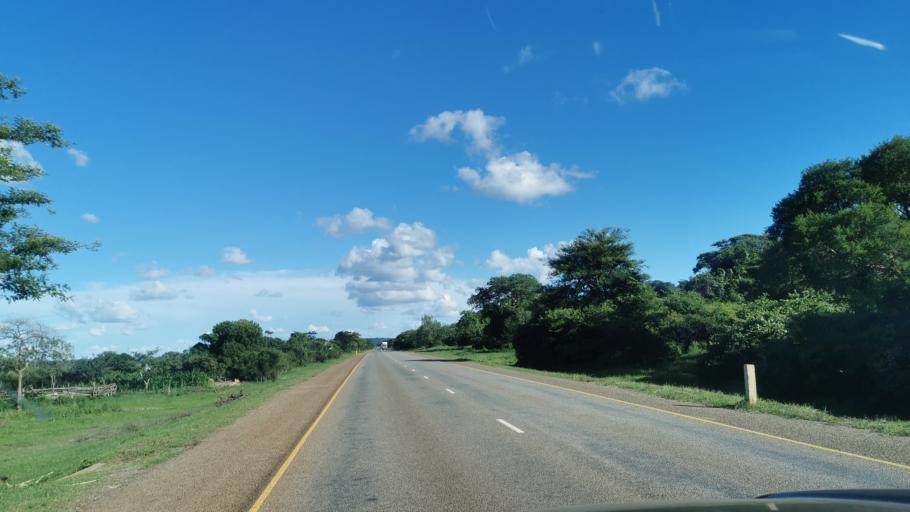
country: TZ
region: Geita
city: Masumbwe
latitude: -3.7187
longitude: 32.2940
